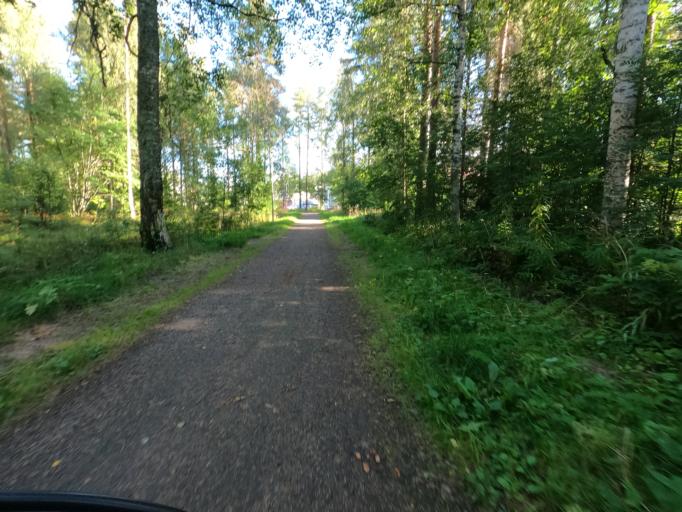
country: FI
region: North Karelia
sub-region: Joensuu
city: Joensuu
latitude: 62.6126
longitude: 29.7590
